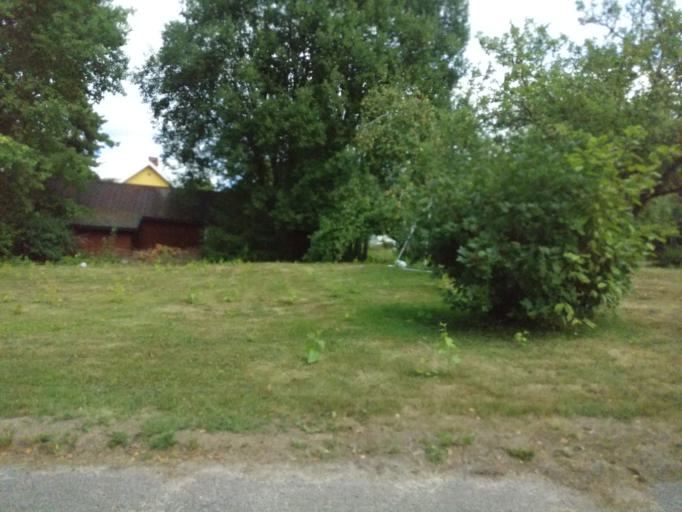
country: SE
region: Vaermland
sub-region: Hagfors Kommun
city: Hagfors
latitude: 60.0219
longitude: 13.6975
